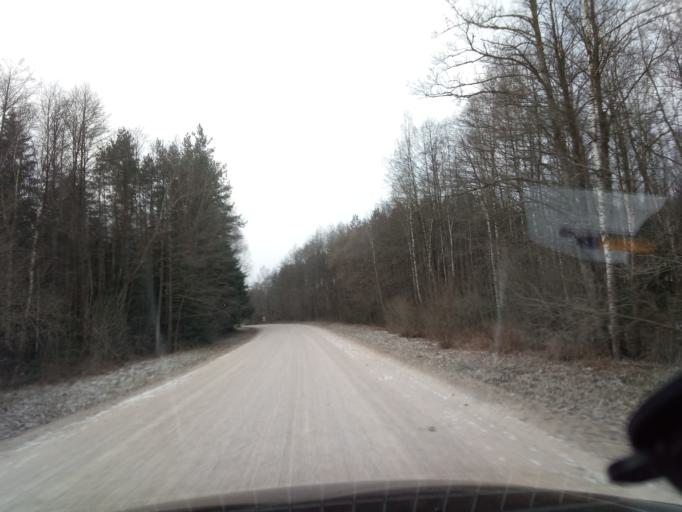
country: LT
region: Alytaus apskritis
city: Varena
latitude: 54.1202
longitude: 24.6403
